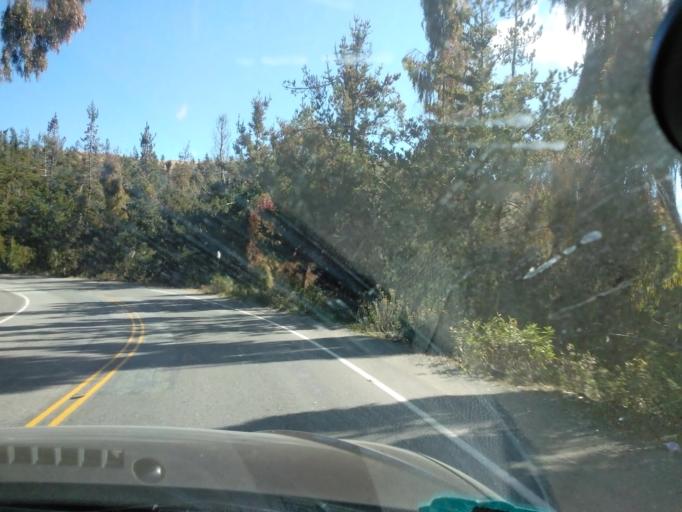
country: PE
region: Apurimac
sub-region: Provincia de Abancay
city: Cachora
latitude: -13.5650
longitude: -72.8211
